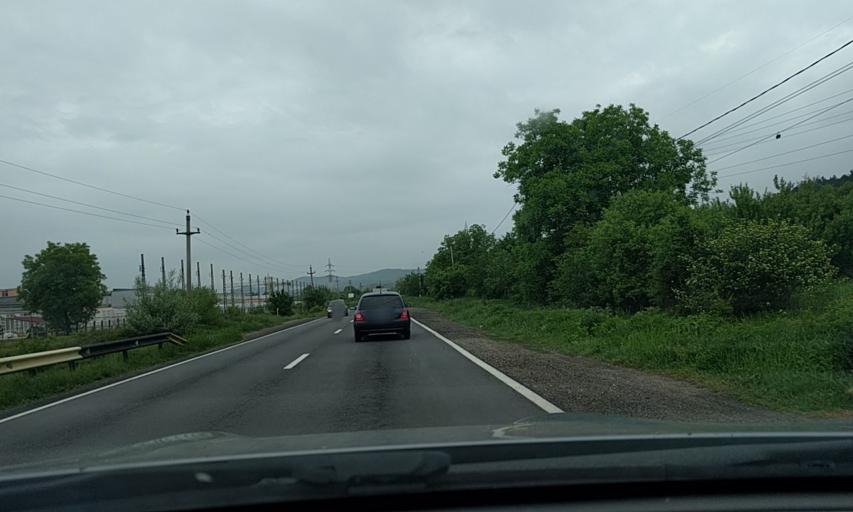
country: RO
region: Dambovita
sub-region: Comuna Vulcana-Pandele
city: Vulcana-Pandele
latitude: 45.0047
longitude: 25.4015
